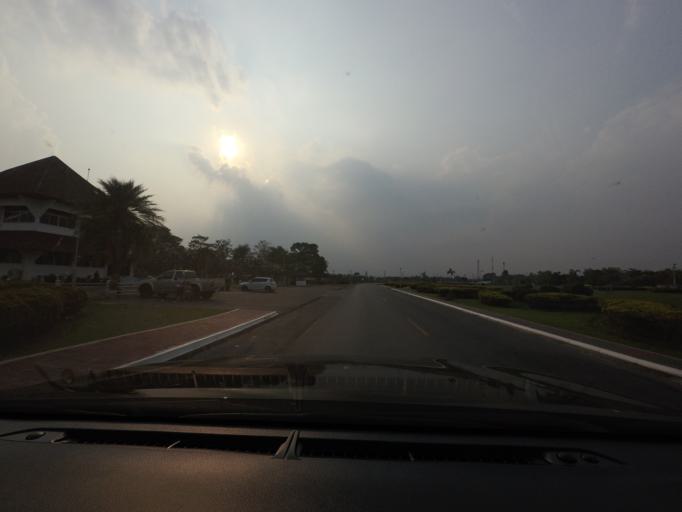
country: TH
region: Sara Buri
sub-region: Amphoe Wang Muang
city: Wang Muang
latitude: 14.8616
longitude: 101.0651
